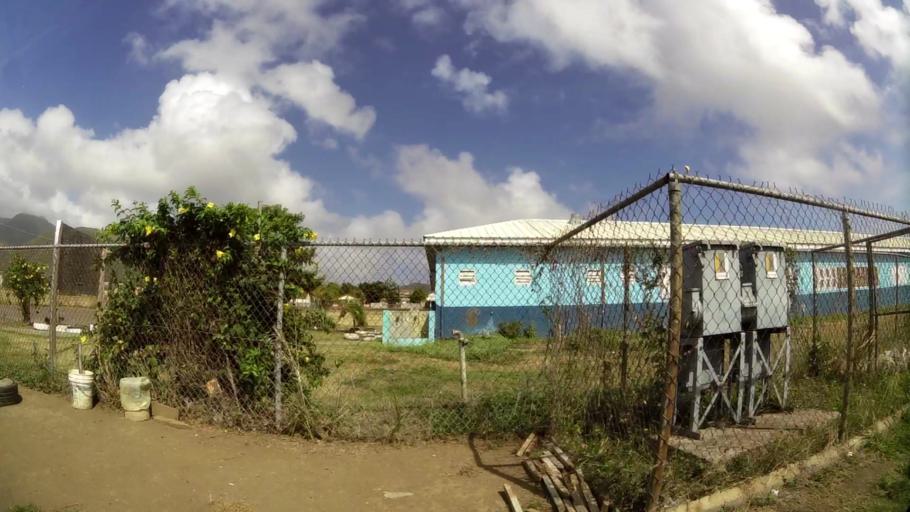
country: KN
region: Saint George Basseterre
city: Basseterre
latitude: 17.3030
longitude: -62.7218
